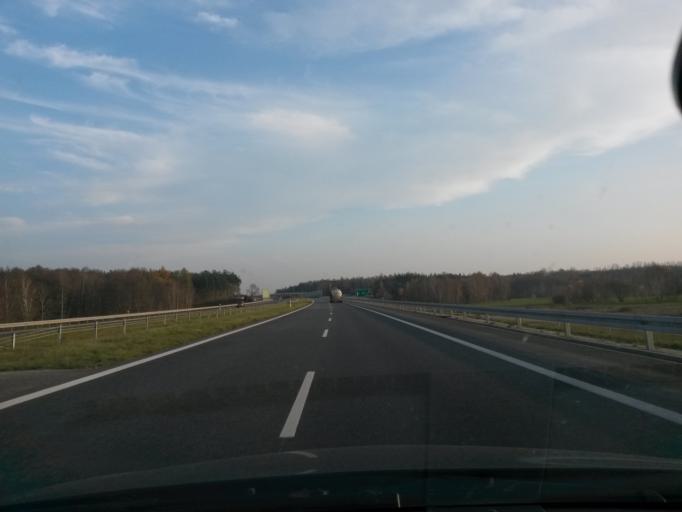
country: PL
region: Lodz Voivodeship
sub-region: Powiat wieruszowski
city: Wieruszow
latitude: 51.3135
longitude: 18.1715
